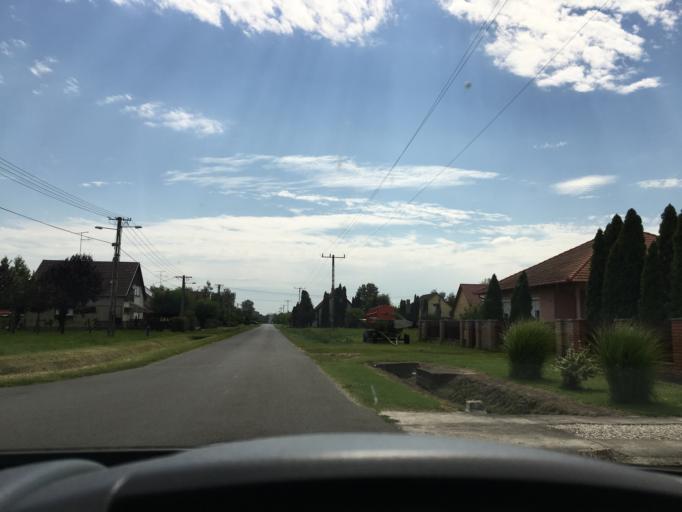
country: HU
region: Csongrad
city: Morahalom
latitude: 46.2111
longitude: 19.8754
